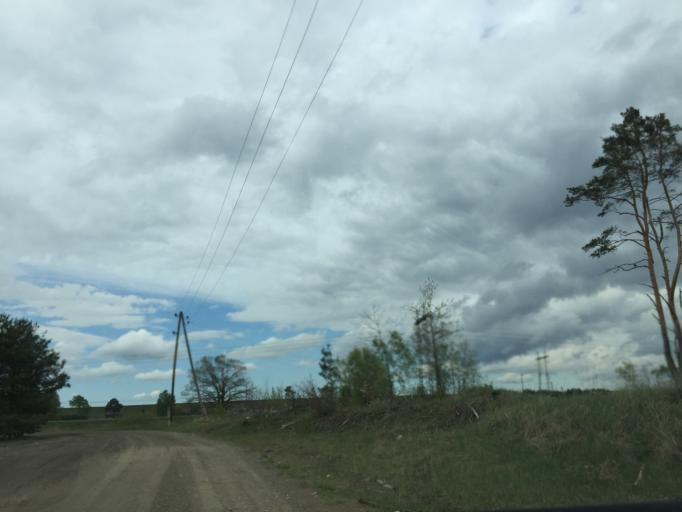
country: LV
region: Kekava
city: Kekava
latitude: 56.8168
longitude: 24.2935
